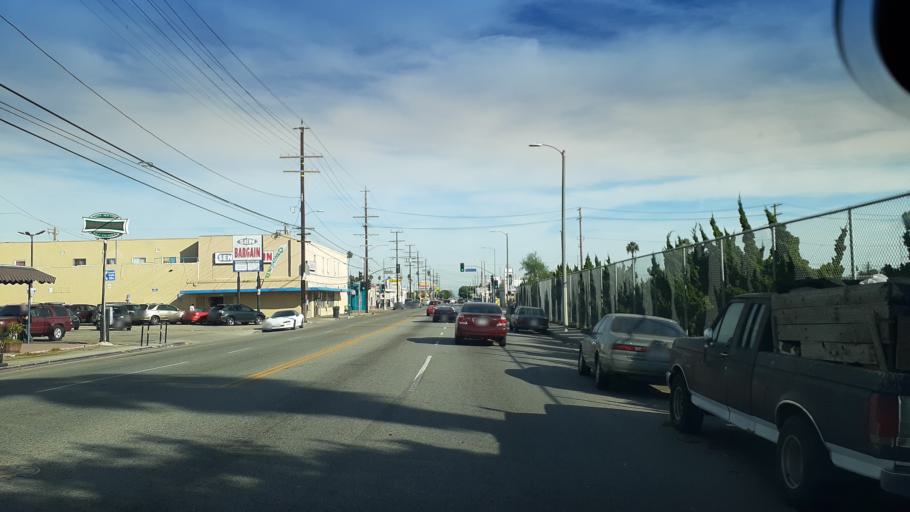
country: US
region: California
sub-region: Los Angeles County
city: Lomita
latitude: 33.7795
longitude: -118.2700
